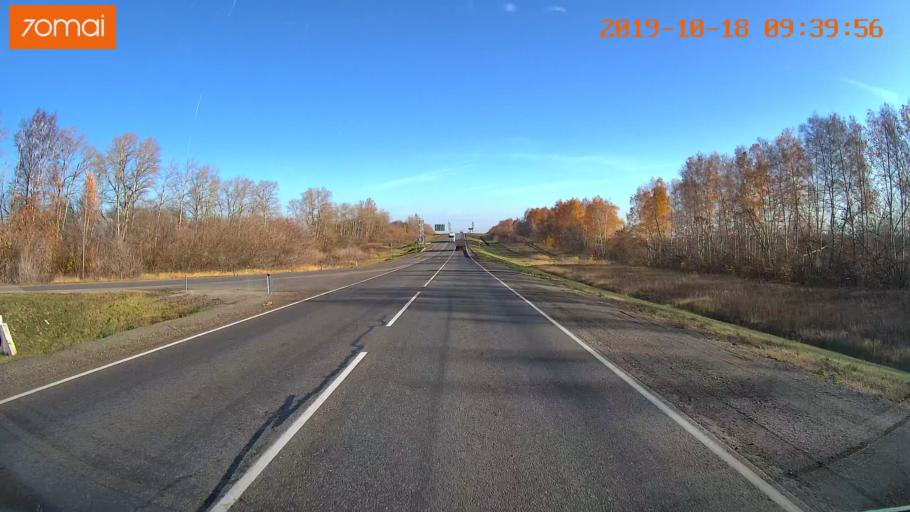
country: RU
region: Tula
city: Yefremov
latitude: 53.2586
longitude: 38.1414
